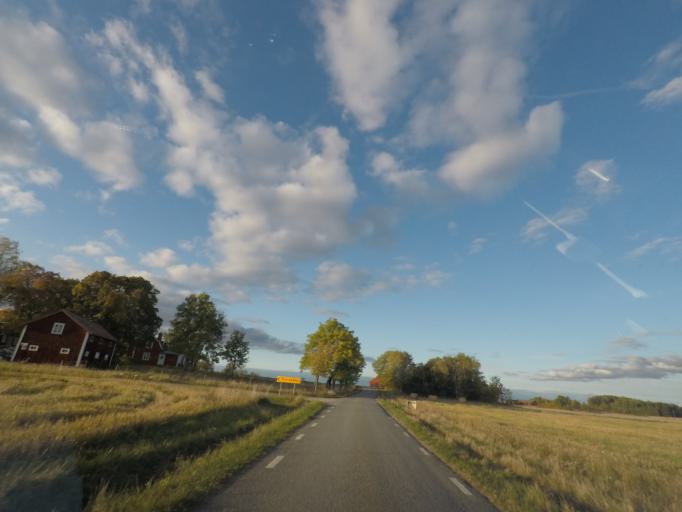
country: SE
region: Vaestmanland
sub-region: Kungsors Kommun
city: Kungsoer
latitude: 59.5167
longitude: 16.1127
